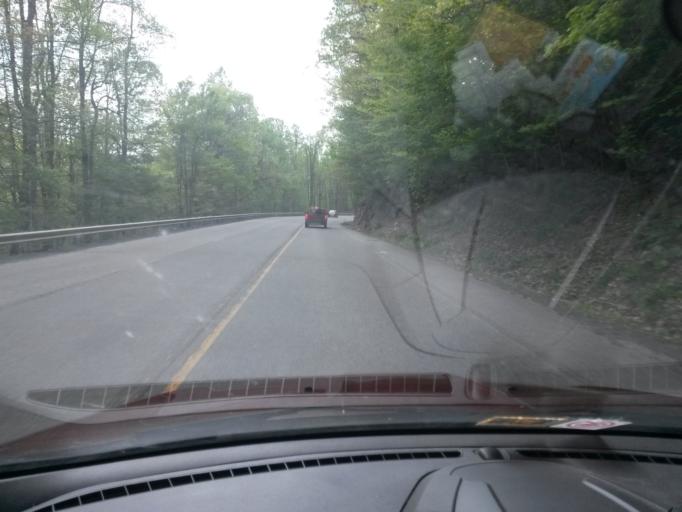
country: US
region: West Virginia
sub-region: Greenbrier County
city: Rainelle
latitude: 38.0163
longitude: -80.7256
